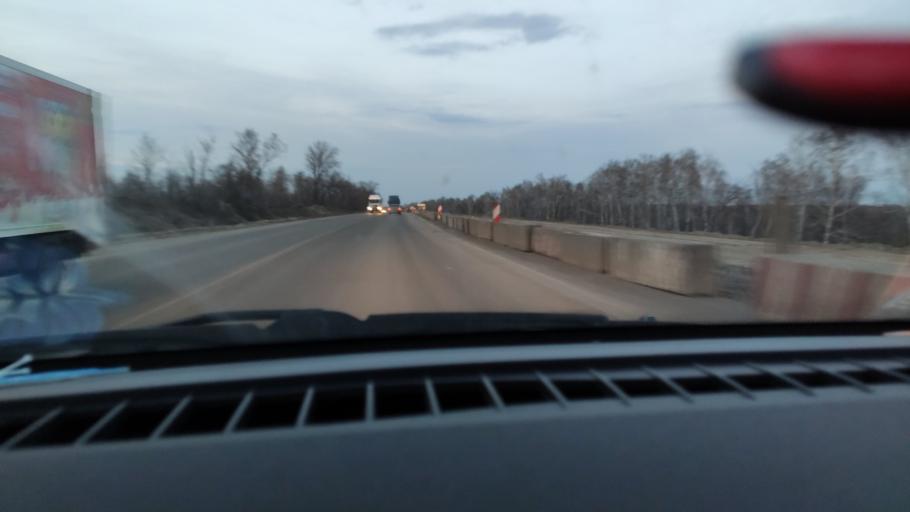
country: RU
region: Saratov
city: Sinodskoye
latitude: 52.0236
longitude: 46.7106
